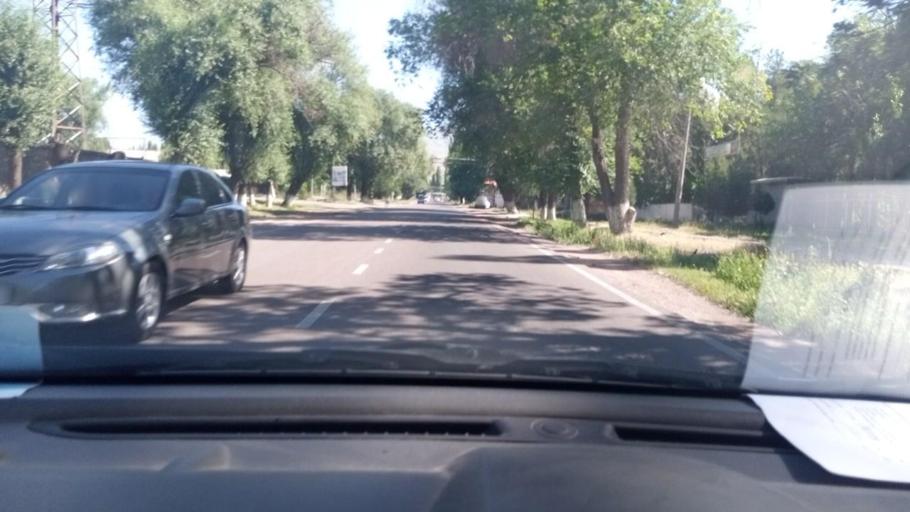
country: UZ
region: Toshkent
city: Angren
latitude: 41.0351
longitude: 70.0928
